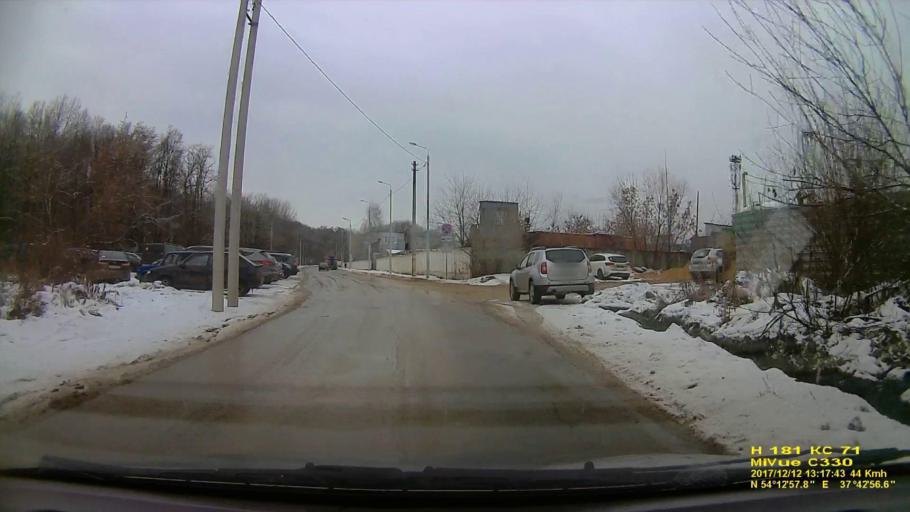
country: RU
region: Tula
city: Tula
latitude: 54.2161
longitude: 37.7158
